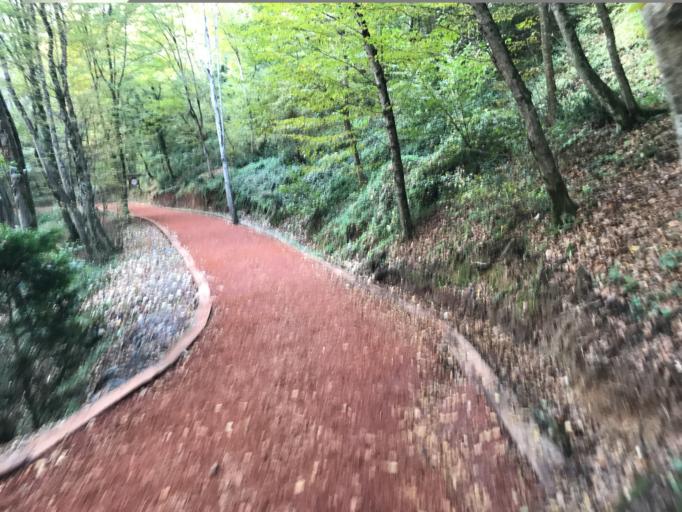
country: TR
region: Istanbul
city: Kemerburgaz
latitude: 41.1734
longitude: 28.9575
